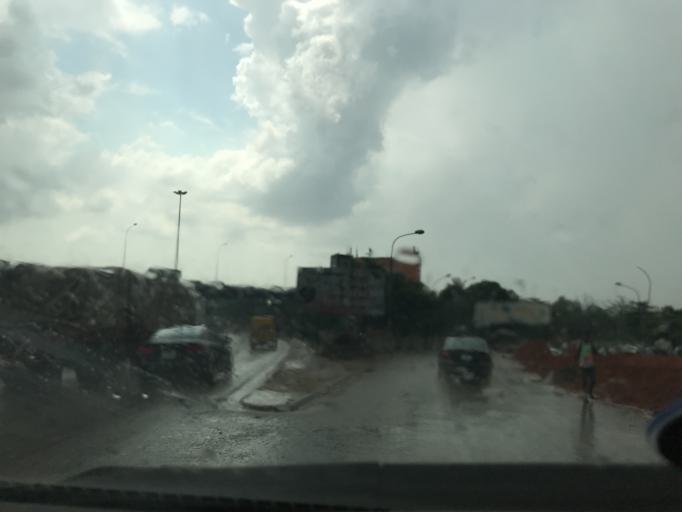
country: NG
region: Lagos
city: Oshodi
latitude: 6.5499
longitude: 3.3389
